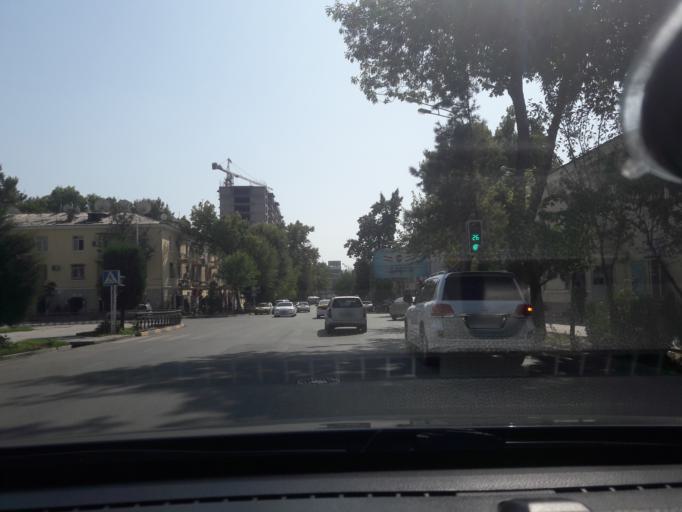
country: TJ
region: Dushanbe
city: Dushanbe
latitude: 38.5660
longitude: 68.7999
